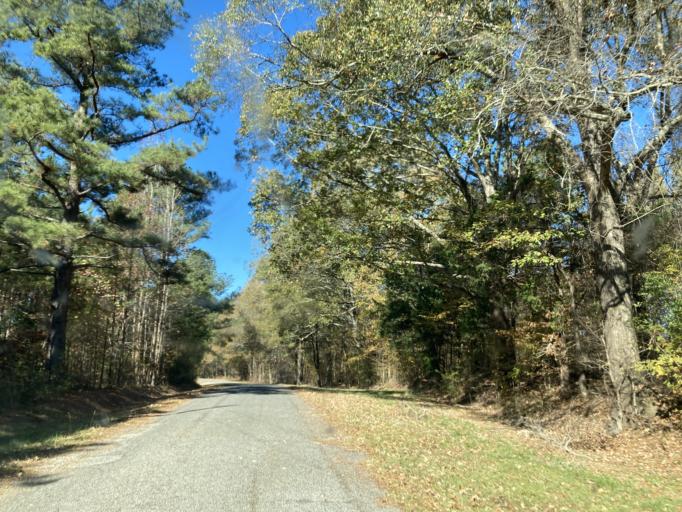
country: US
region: Mississippi
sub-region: Hinds County
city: Lynchburg
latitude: 32.5720
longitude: -90.5459
